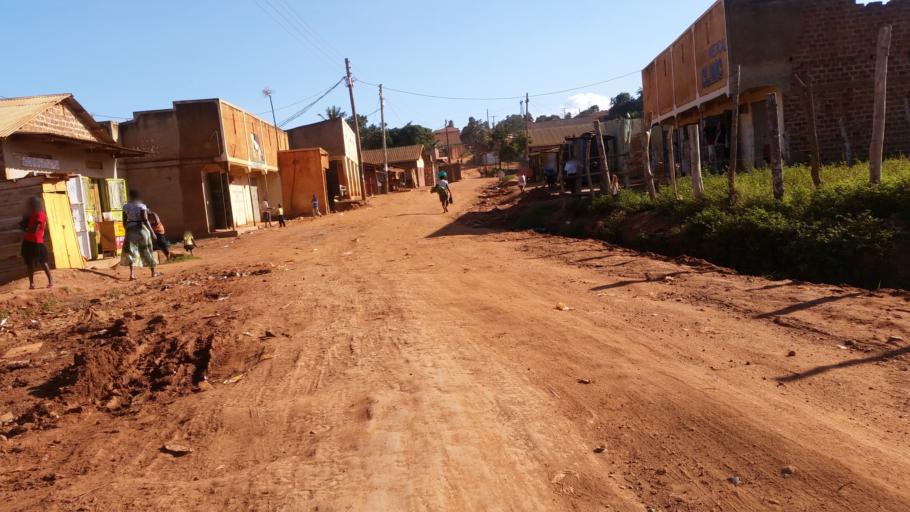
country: UG
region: Central Region
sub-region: Wakiso District
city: Kireka
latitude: 0.3254
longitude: 32.6464
